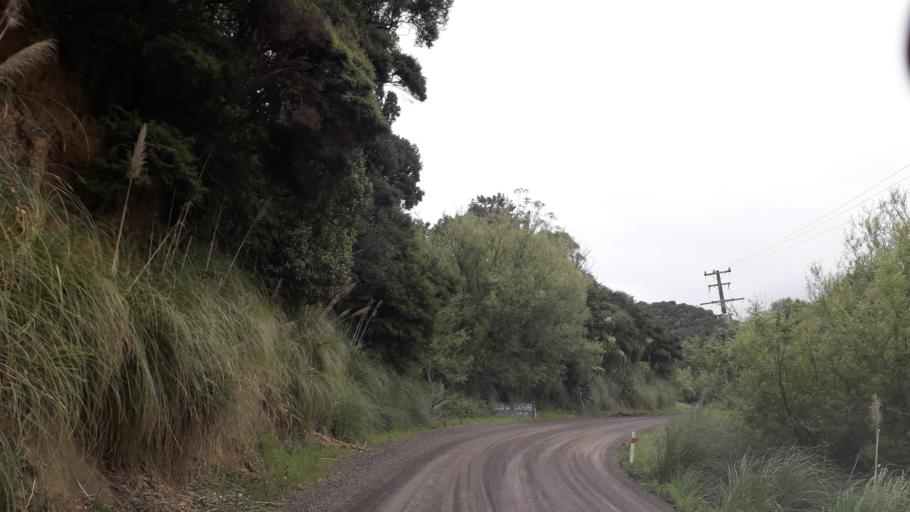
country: NZ
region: Northland
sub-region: Far North District
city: Ahipara
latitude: -35.4377
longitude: 173.3078
